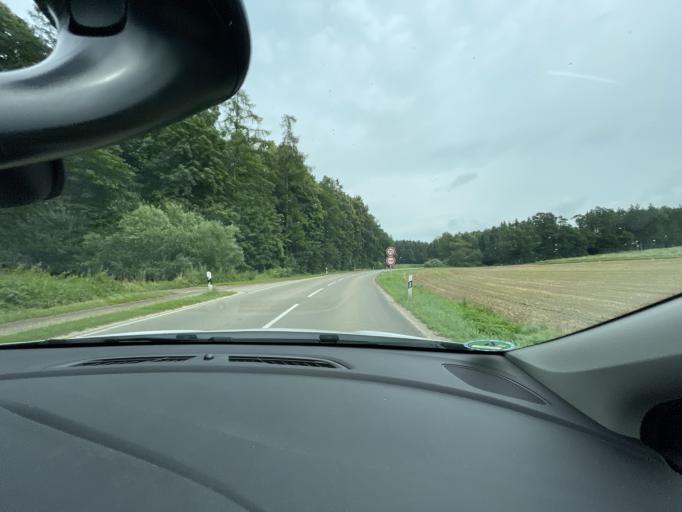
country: DE
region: Bavaria
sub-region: Swabia
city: Thierhaupten
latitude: 48.5637
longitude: 10.9461
